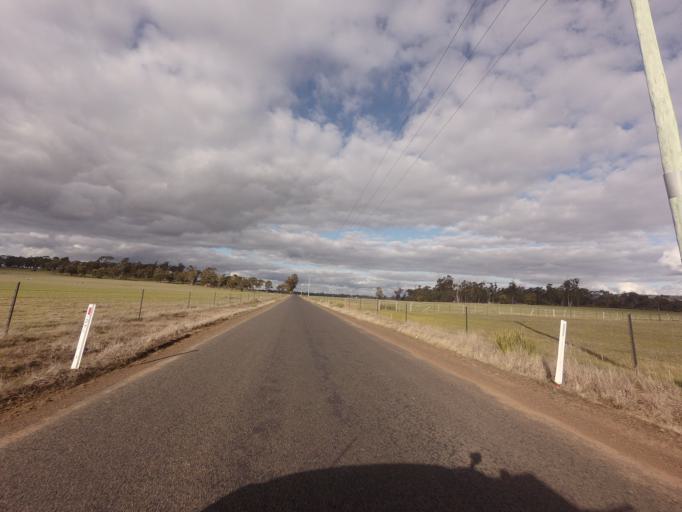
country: AU
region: Tasmania
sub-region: Northern Midlands
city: Longford
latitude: -41.8614
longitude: 147.2581
